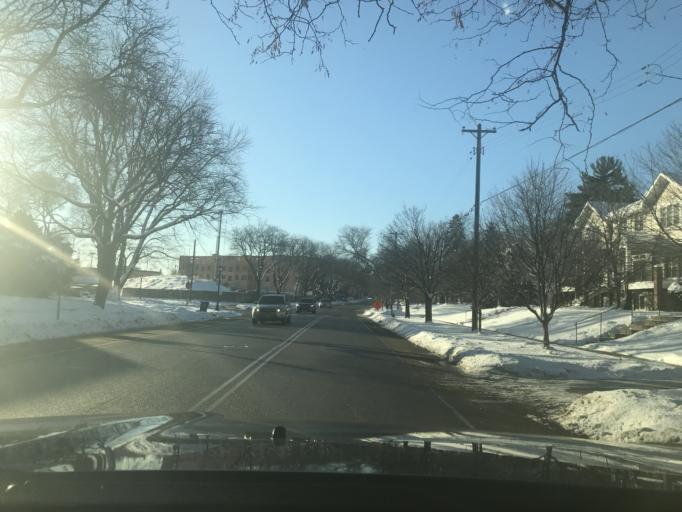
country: US
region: Minnesota
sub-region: Dakota County
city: Mendota Heights
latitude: 44.9161
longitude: -93.1483
